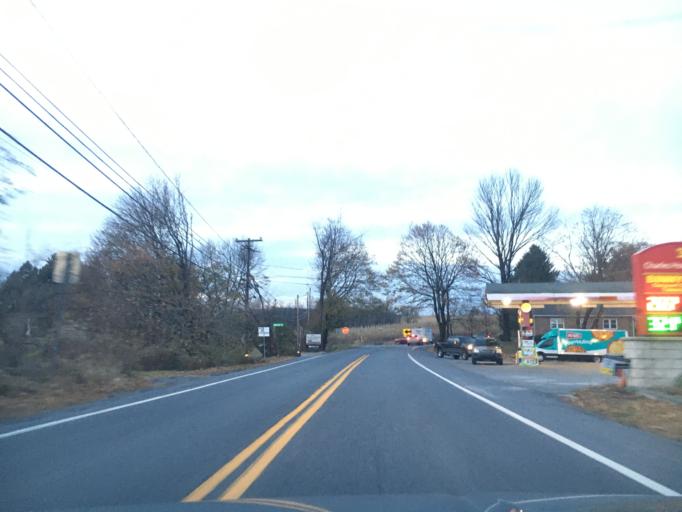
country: US
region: Pennsylvania
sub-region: Lehigh County
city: Schnecksville
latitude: 40.6779
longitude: -75.5707
